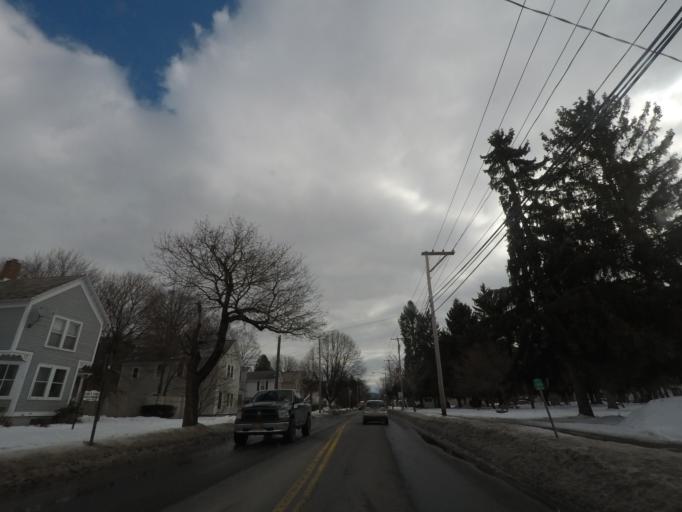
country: US
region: New York
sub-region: Washington County
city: Greenwich
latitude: 43.0943
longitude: -73.5057
